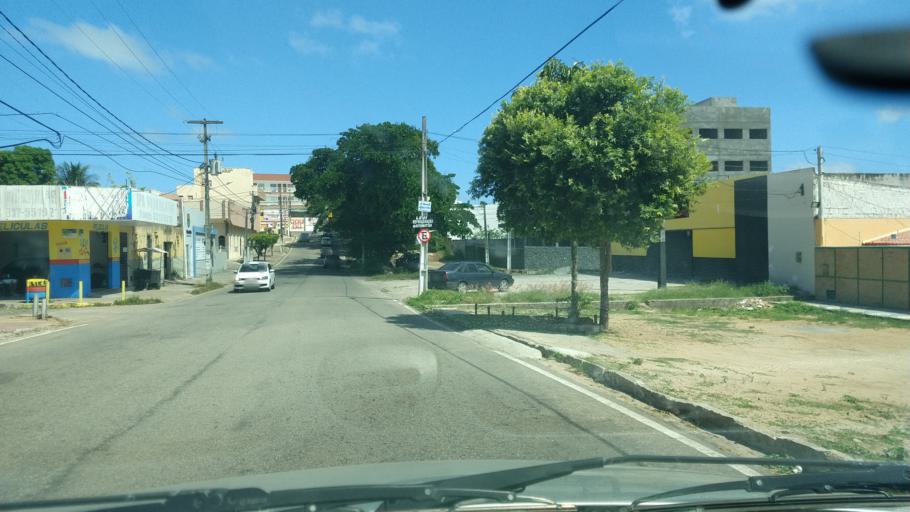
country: BR
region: Rio Grande do Norte
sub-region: Natal
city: Natal
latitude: -5.8590
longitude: -35.2070
